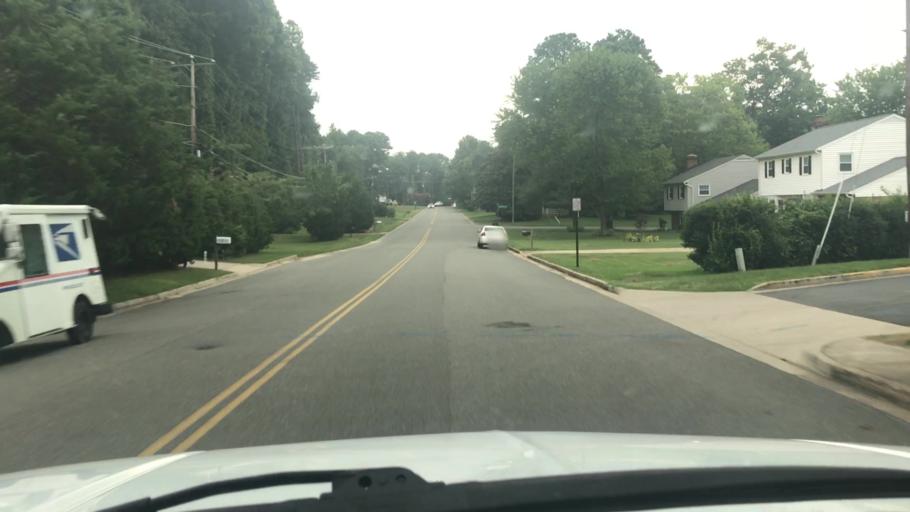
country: US
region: Virginia
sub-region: Henrico County
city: Tuckahoe
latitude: 37.6021
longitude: -77.5857
